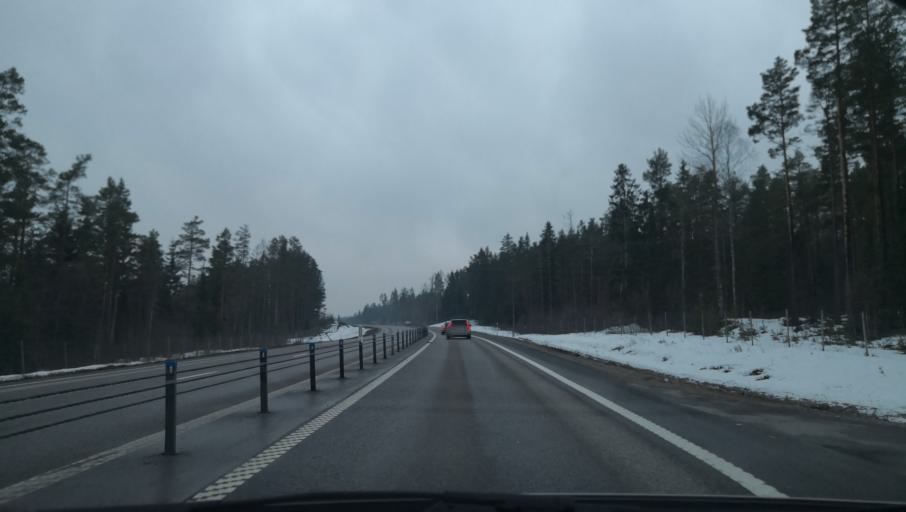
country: SE
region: Vaesternorrland
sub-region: Sundsvalls Kommun
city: Njurundabommen
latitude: 62.1117
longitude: 17.3195
